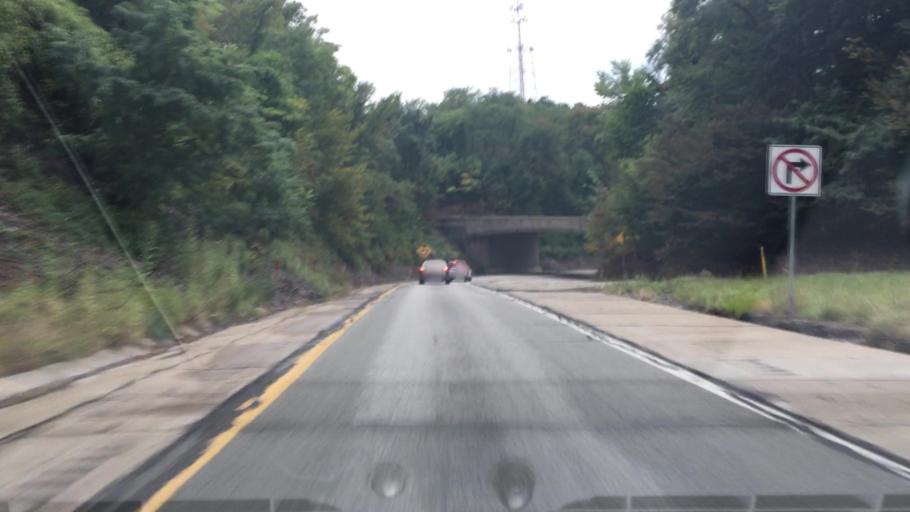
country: US
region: Pennsylvania
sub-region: Allegheny County
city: Edgewood
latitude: 40.4351
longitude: -79.8663
